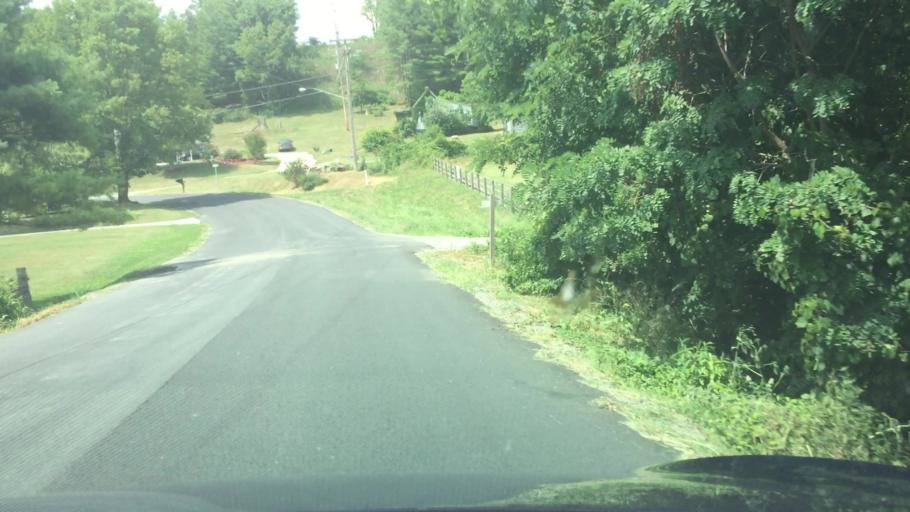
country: US
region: Virginia
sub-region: Wythe County
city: Wytheville
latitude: 36.9379
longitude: -81.0739
